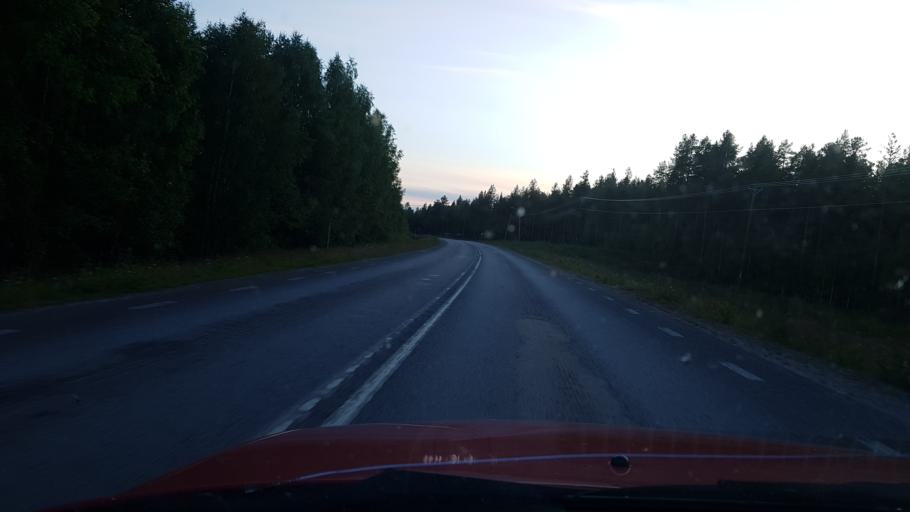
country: SE
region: Norrbotten
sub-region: Alvsbyns Kommun
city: AElvsbyn
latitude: 65.6931
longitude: 20.6790
